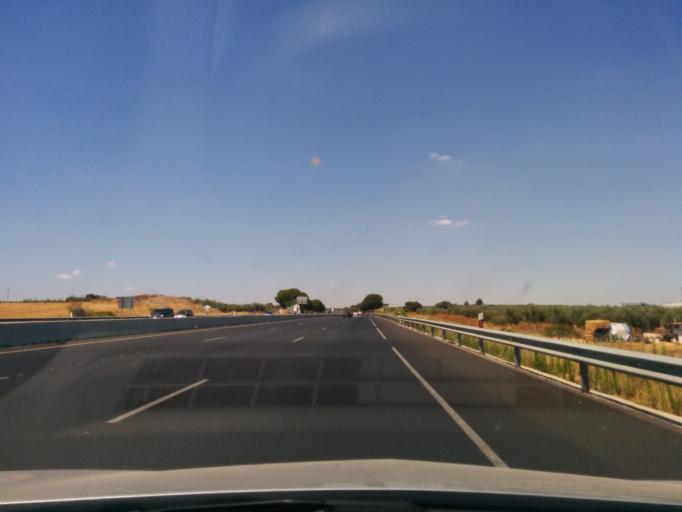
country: ES
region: Andalusia
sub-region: Provincia de Sevilla
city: Umbrete
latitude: 37.3586
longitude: -6.1545
